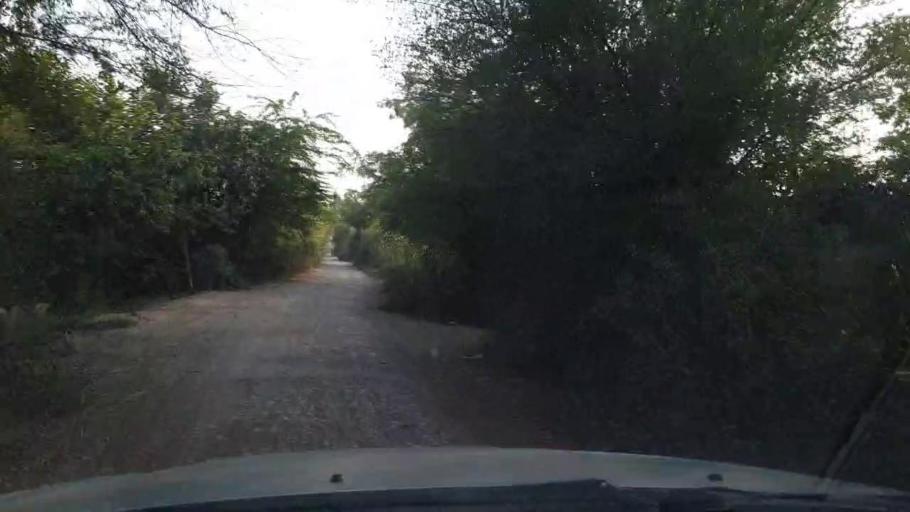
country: PK
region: Sindh
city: Tando Muhammad Khan
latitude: 25.0080
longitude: 68.4358
